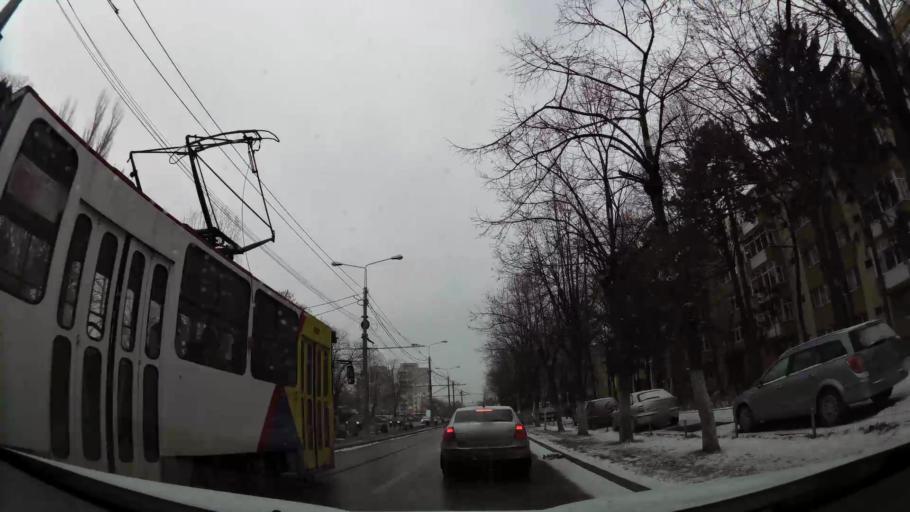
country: RO
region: Prahova
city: Ploiesti
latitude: 44.9598
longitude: 26.0106
